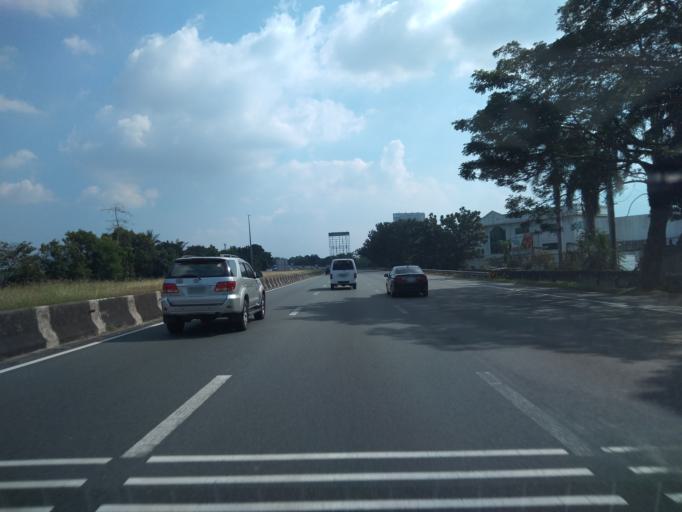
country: PH
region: Calabarzon
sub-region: Province of Laguna
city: San Pedro
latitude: 14.3523
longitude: 121.0457
